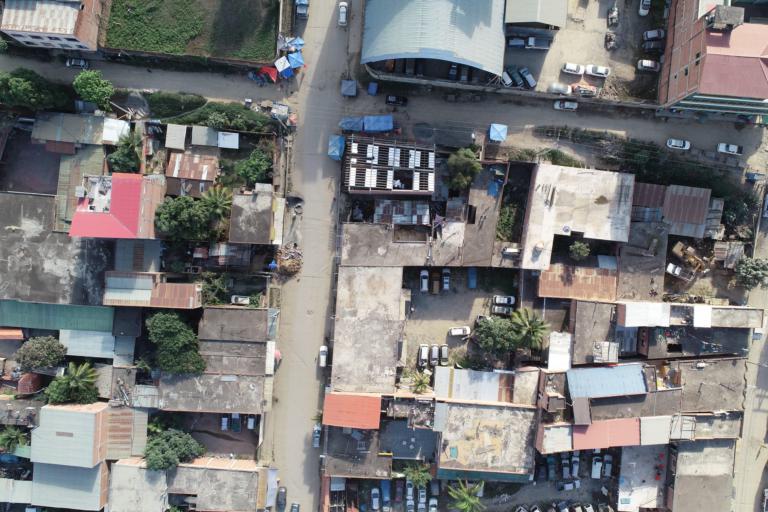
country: BO
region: La Paz
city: Coroico
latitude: -15.8354
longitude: -67.5629
